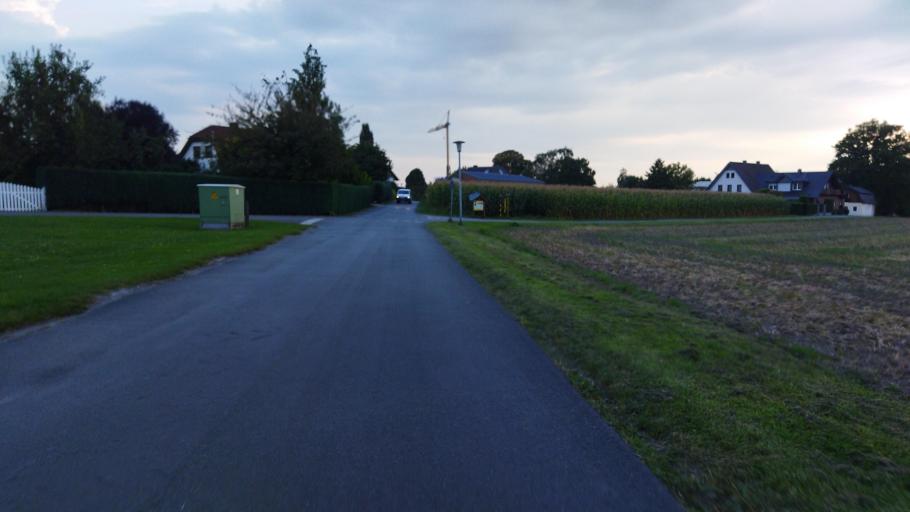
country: DE
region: Lower Saxony
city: Bad Iburg
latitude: 52.1403
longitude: 8.0521
